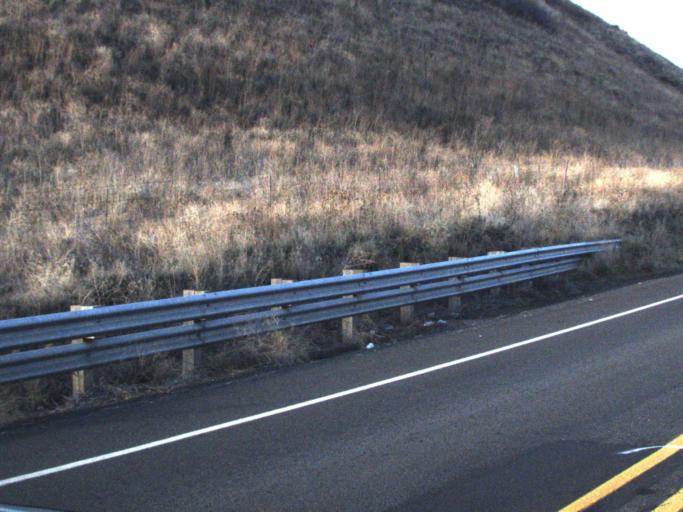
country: US
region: Washington
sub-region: Garfield County
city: Pomeroy
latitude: 46.6720
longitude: -117.8107
